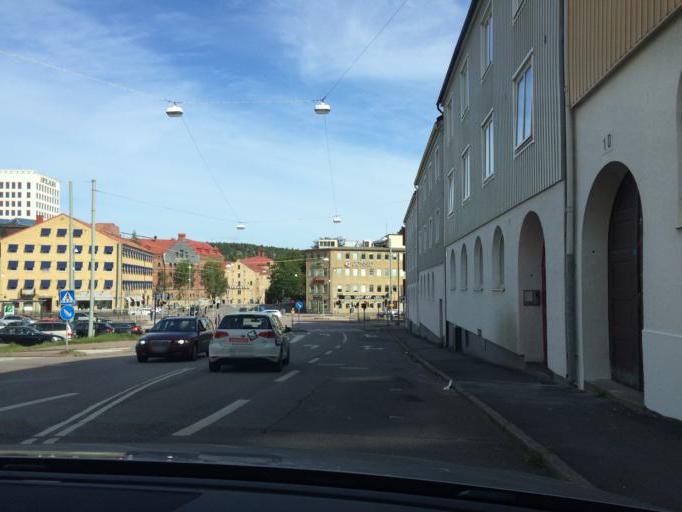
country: SE
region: Vaestra Goetaland
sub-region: Goteborg
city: Goeteborg
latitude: 57.6869
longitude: 11.9957
